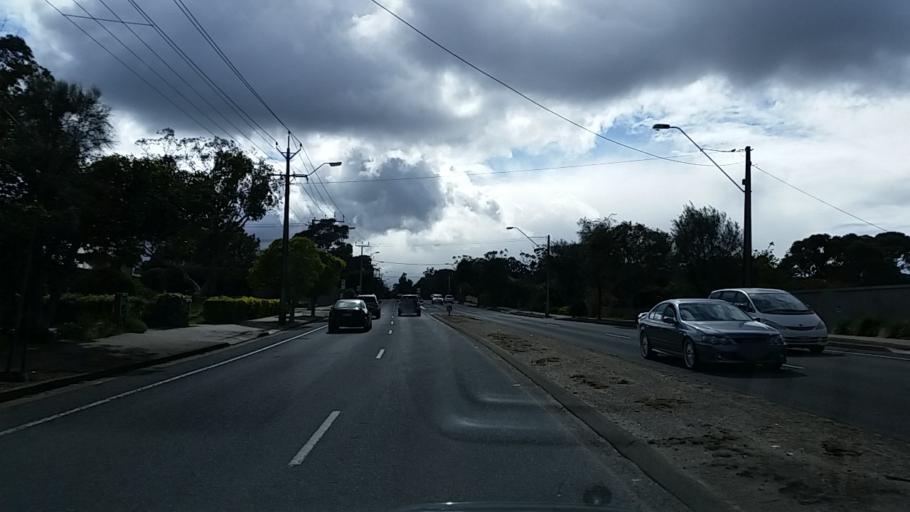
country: AU
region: South Australia
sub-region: Mitcham
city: Blackwood
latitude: -35.0282
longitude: 138.5958
